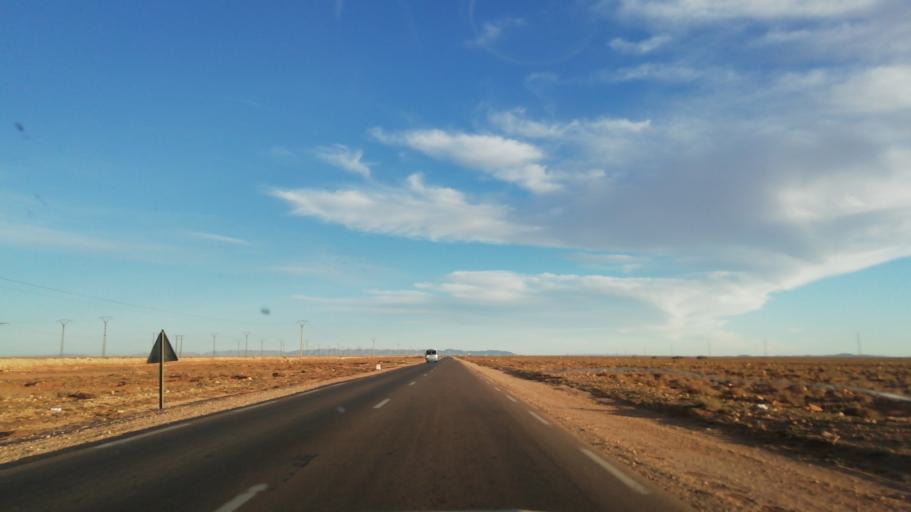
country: DZ
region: Wilaya de Naama
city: Naama
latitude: 33.7430
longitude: -0.7768
